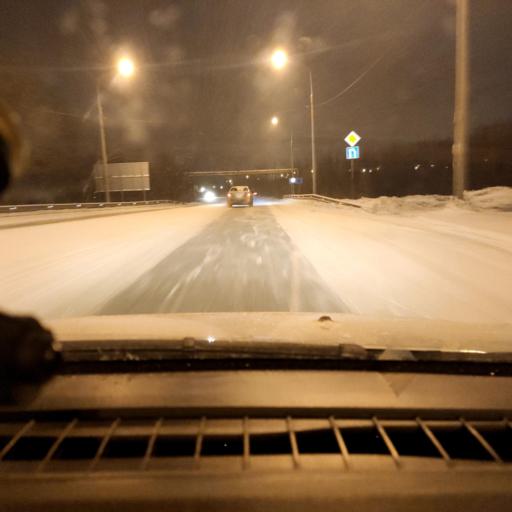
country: RU
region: Samara
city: Otradnyy
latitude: 53.3504
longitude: 51.3260
